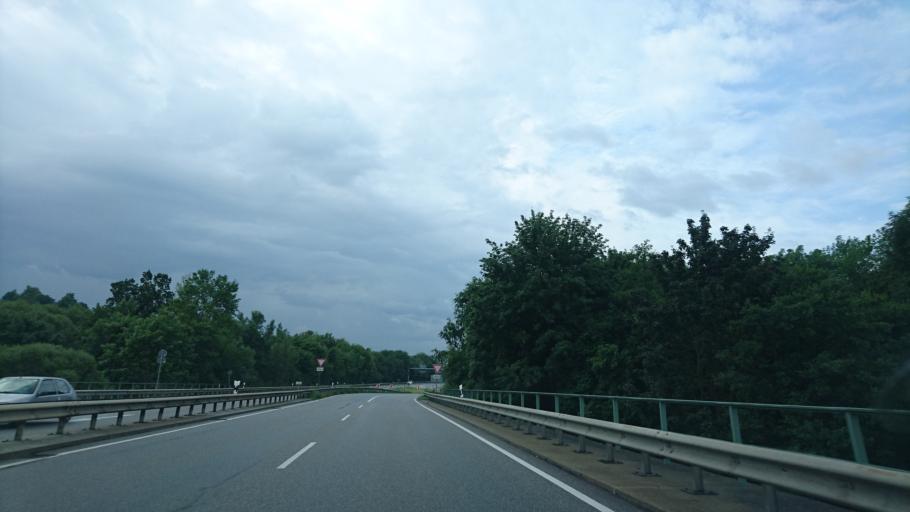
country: DE
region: Bavaria
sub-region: Upper Palatinate
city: Lappersdorf
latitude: 49.0458
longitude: 12.0983
